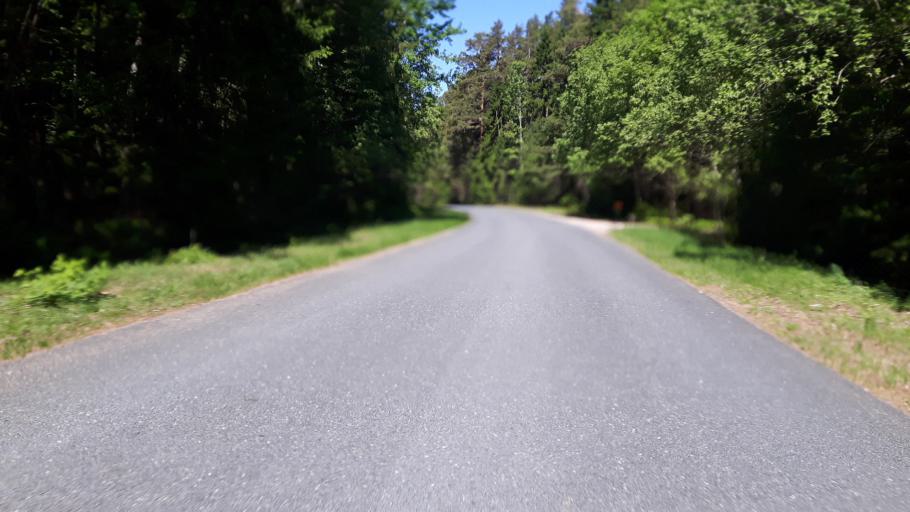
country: EE
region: Harju
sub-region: Loksa linn
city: Loksa
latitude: 59.5696
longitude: 25.6241
